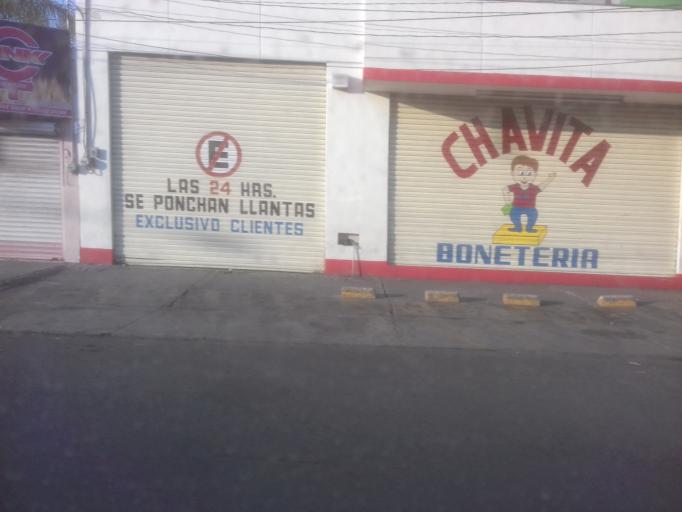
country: MX
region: Aguascalientes
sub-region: Aguascalientes
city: Aguascalientes
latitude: 21.8659
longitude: -102.2980
